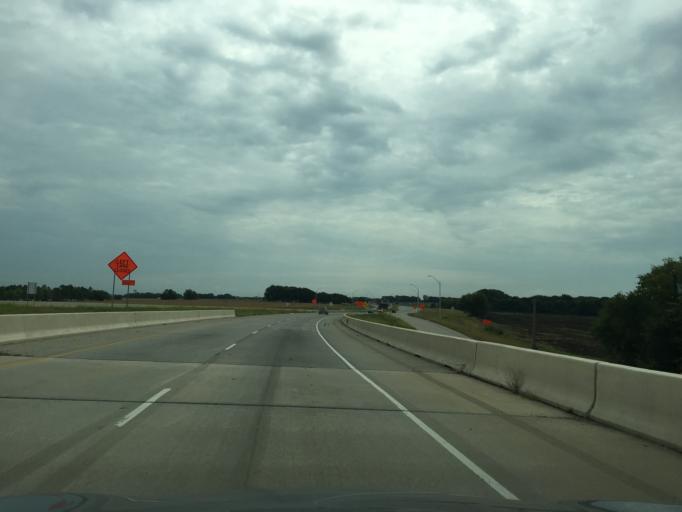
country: US
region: Texas
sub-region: Collin County
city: Melissa
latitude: 33.2645
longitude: -96.5984
